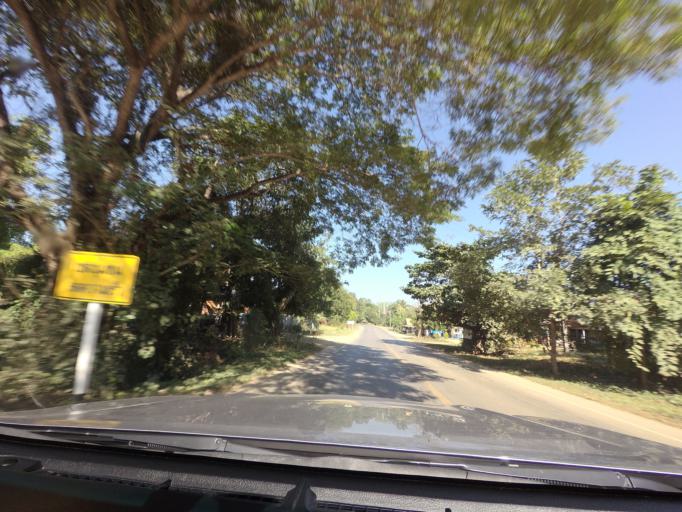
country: TH
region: Sukhothai
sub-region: Amphoe Si Satchanalai
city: Si Satchanalai
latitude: 17.6855
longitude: 99.7082
